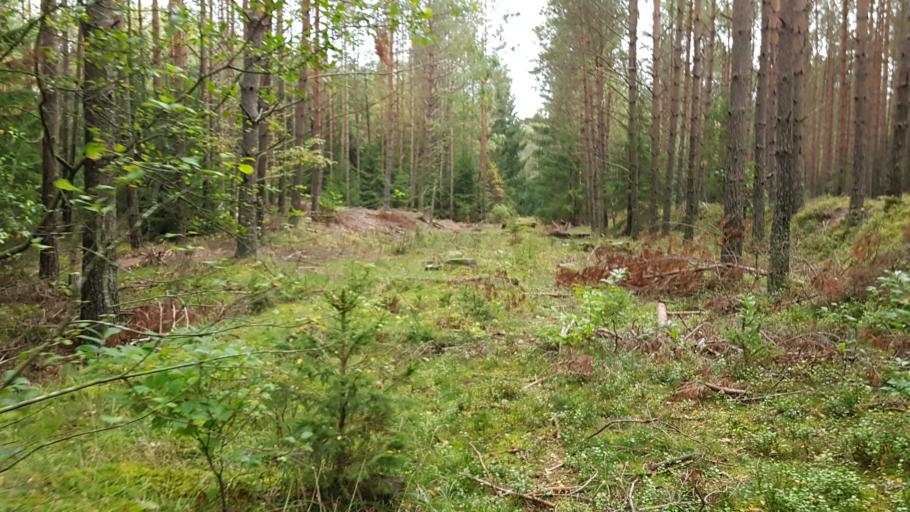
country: PL
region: West Pomeranian Voivodeship
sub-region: Powiat bialogardzki
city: Tychowo
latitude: 54.0452
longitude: 16.3093
